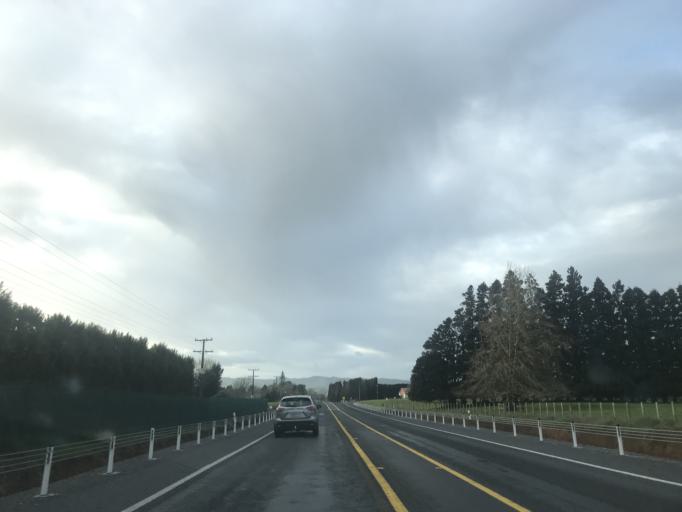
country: NZ
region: Waikato
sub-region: Hauraki District
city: Waihi
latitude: -37.4322
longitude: 175.8721
